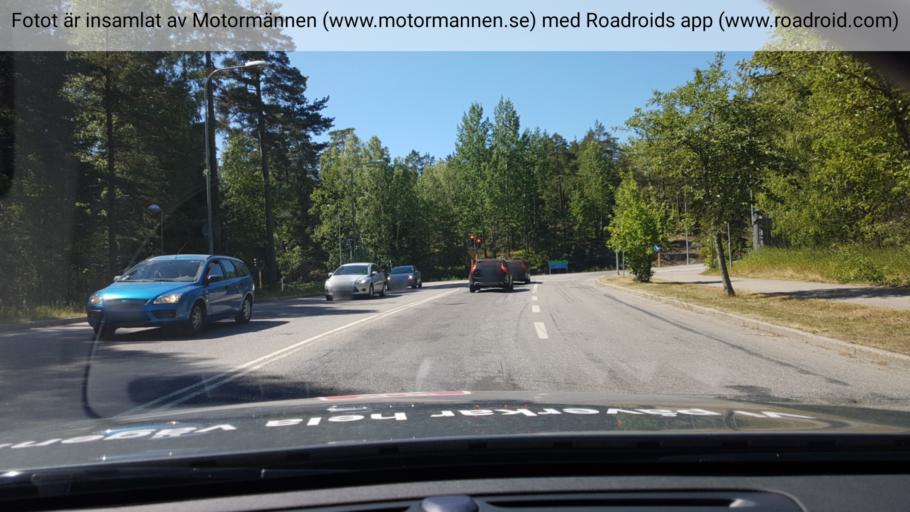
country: SE
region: Stockholm
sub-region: Nacka Kommun
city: Alta
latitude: 59.2340
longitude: 18.1941
